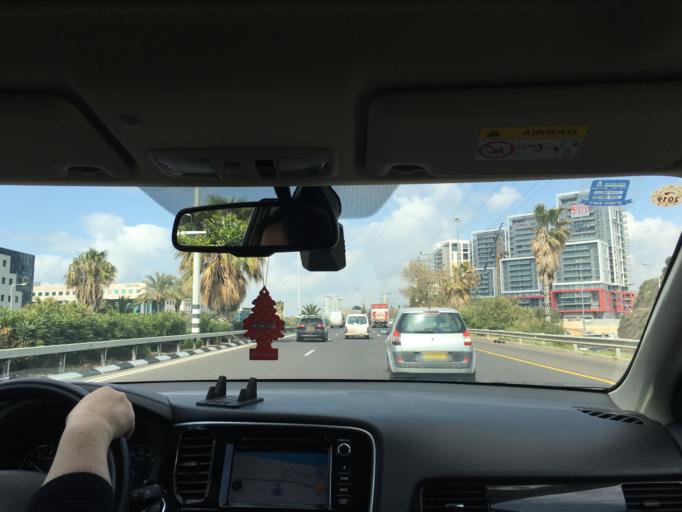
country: IL
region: Tel Aviv
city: Herzliyya
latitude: 32.1589
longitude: 34.8104
